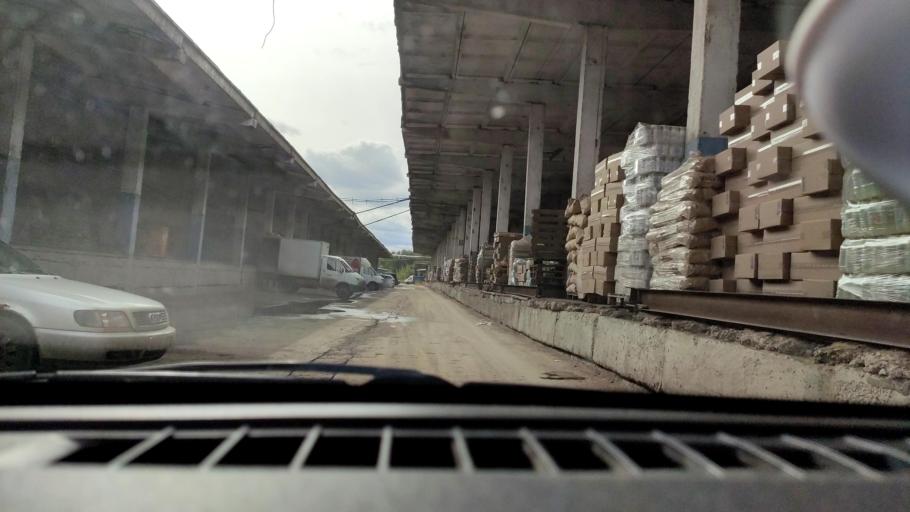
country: RU
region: Samara
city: Samara
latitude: 53.1917
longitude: 50.2358
